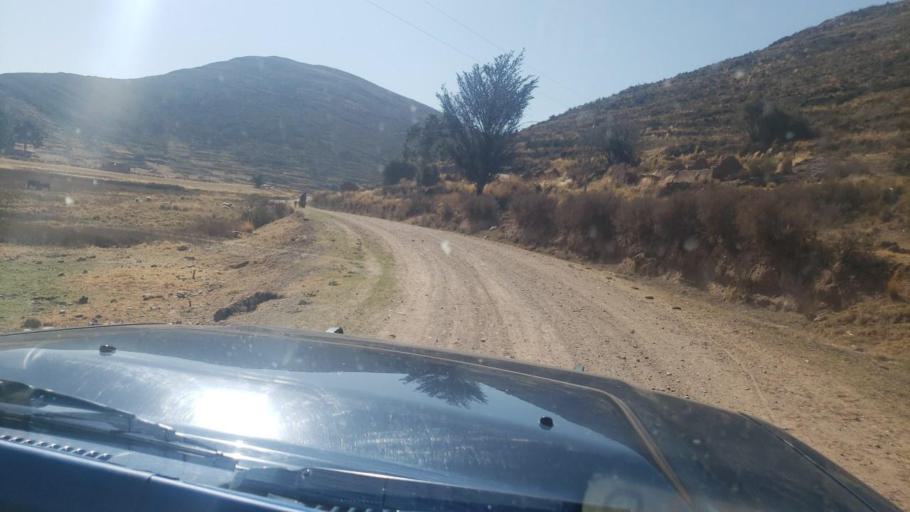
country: BO
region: La Paz
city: Huatajata
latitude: -16.3378
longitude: -68.6770
